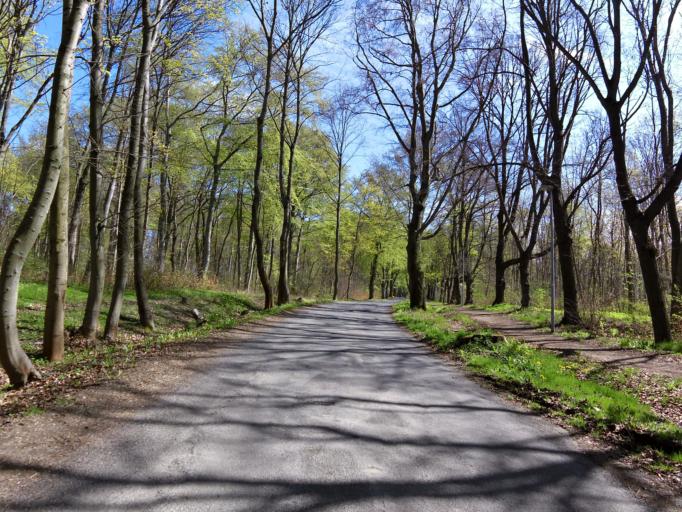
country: DE
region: Thuringia
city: Gotha
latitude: 50.9365
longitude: 10.7201
